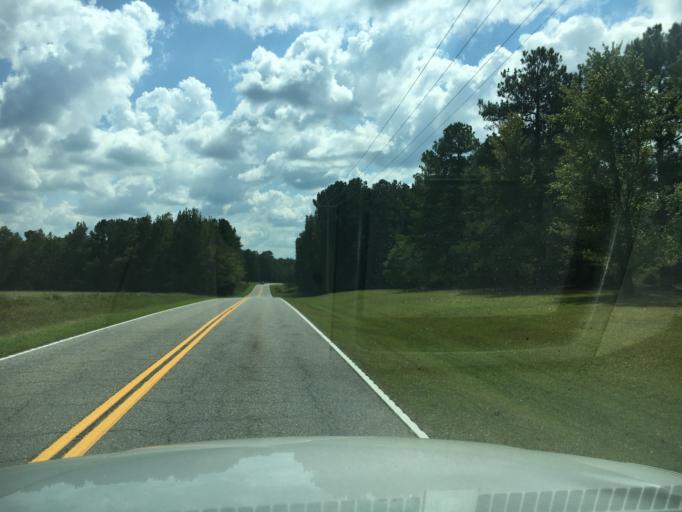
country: US
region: South Carolina
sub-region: Greenwood County
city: Greenwood
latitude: 34.1033
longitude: -82.1297
